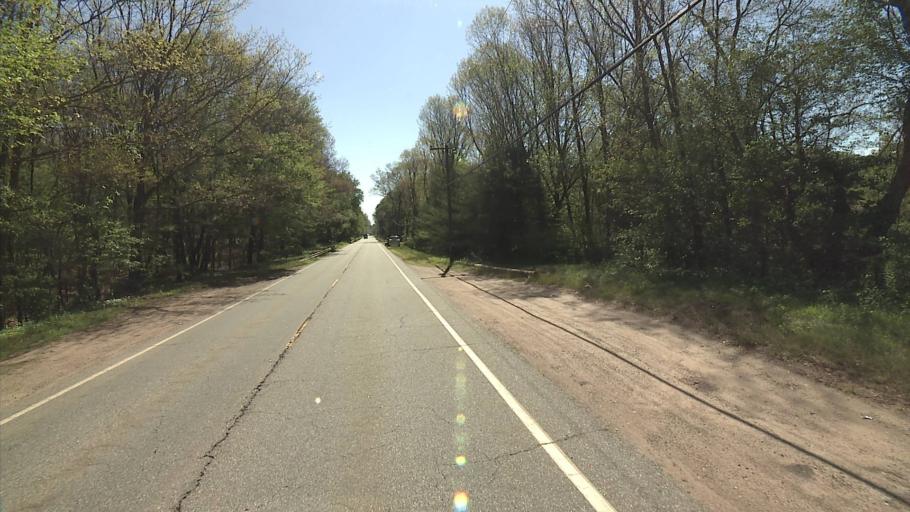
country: US
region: Connecticut
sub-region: Middlesex County
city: East Hampton
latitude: 41.5643
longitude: -72.5264
